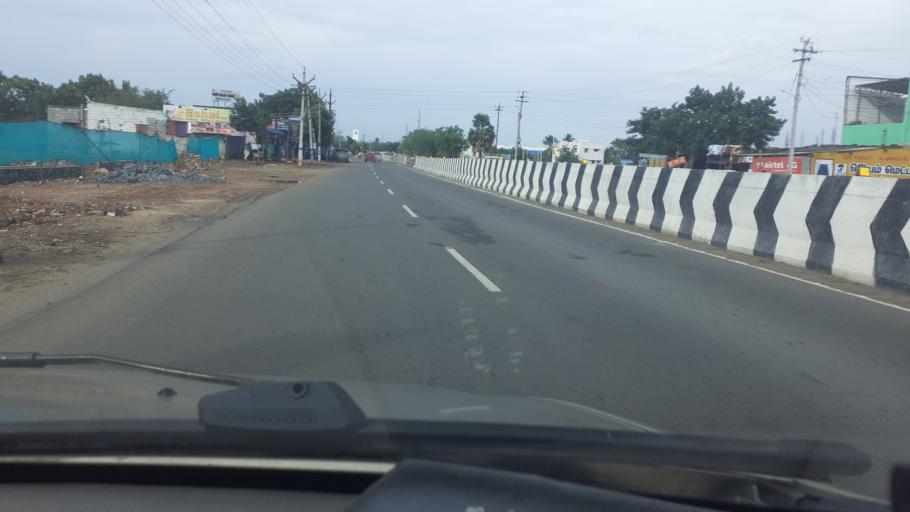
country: IN
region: Tamil Nadu
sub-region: Tirunelveli Kattabo
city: Tirunelveli
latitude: 8.6652
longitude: 77.7163
